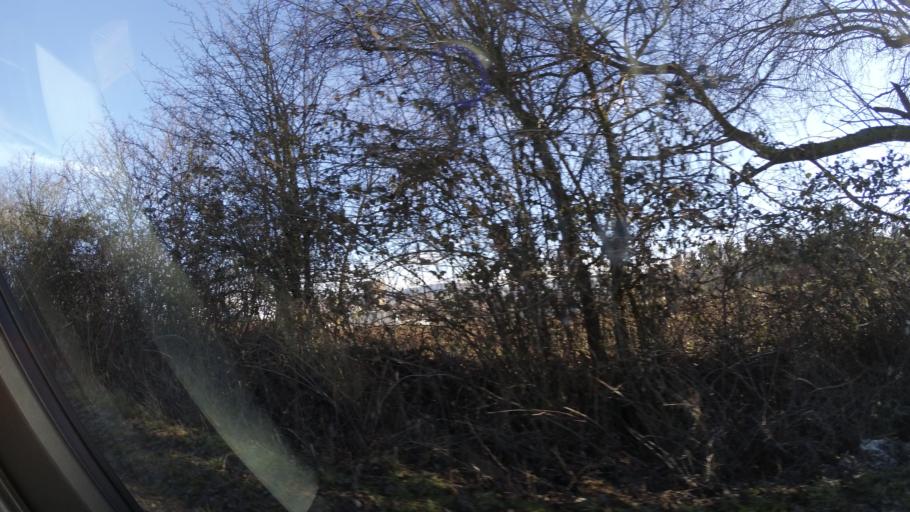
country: DE
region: Saarland
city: Sankt Wendel
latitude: 49.4576
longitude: 7.1432
